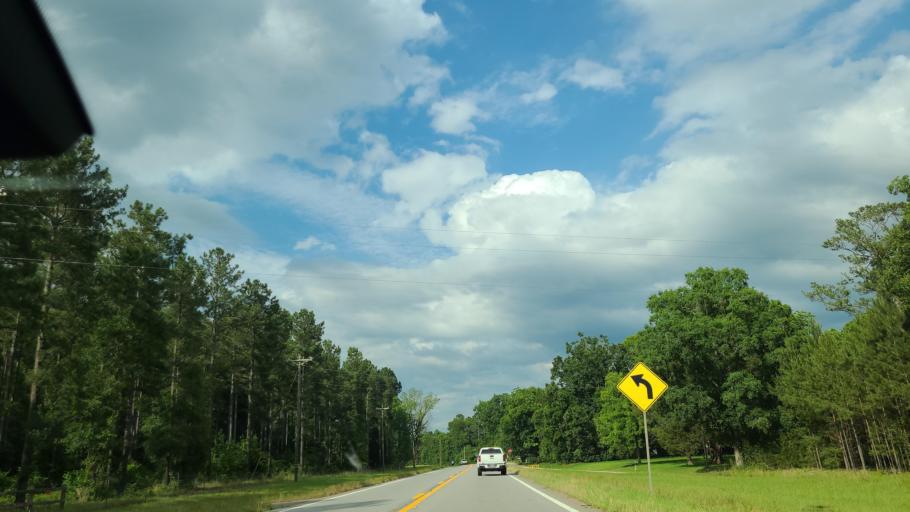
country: US
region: Georgia
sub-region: Jones County
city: Gray
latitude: 33.1593
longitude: -83.4467
